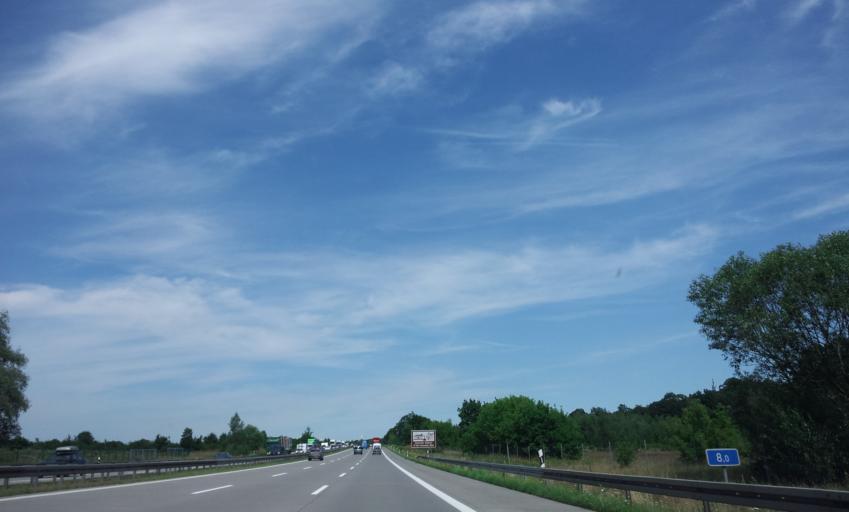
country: DE
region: Berlin
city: Hellersdorf
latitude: 52.5701
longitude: 13.6469
